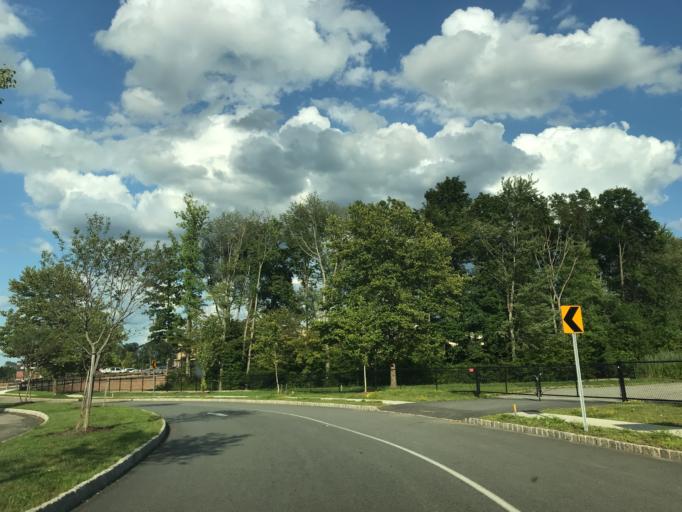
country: US
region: New Jersey
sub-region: Morris County
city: Parsippany
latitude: 40.8384
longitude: -74.4396
